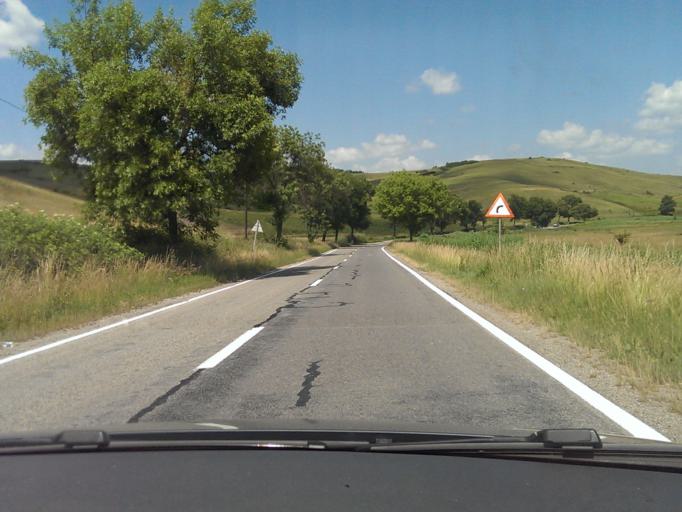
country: RO
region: Cluj
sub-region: Comuna Apahida
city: Apahida
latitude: 46.8091
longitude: 23.7813
